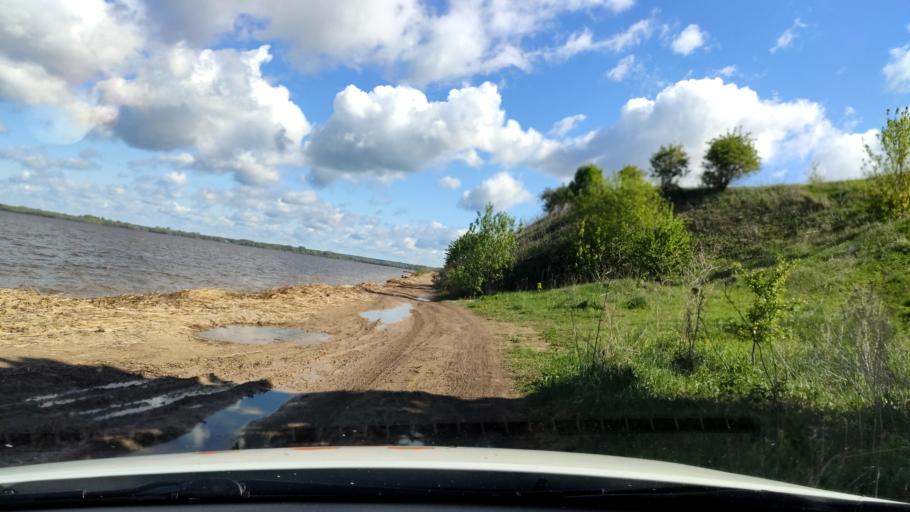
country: RU
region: Tatarstan
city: Sviyazhsk
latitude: 55.7707
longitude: 48.6866
